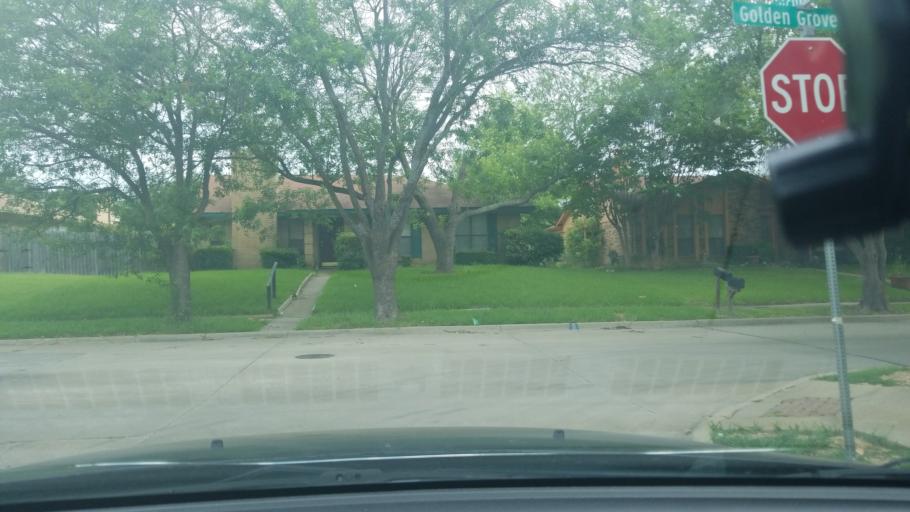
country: US
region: Texas
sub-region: Dallas County
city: Mesquite
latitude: 32.7851
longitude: -96.6462
